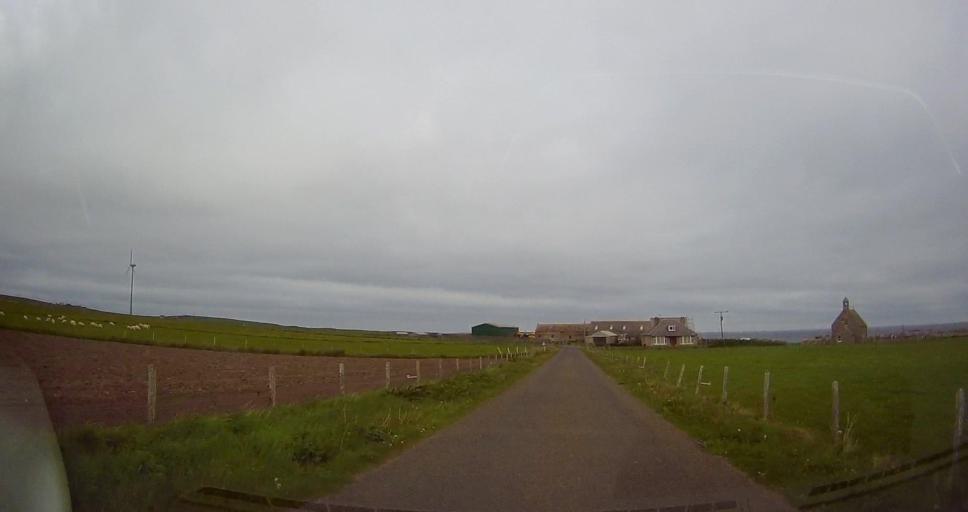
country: GB
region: Scotland
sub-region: Orkney Islands
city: Kirkwall
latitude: 58.9419
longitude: -2.7201
